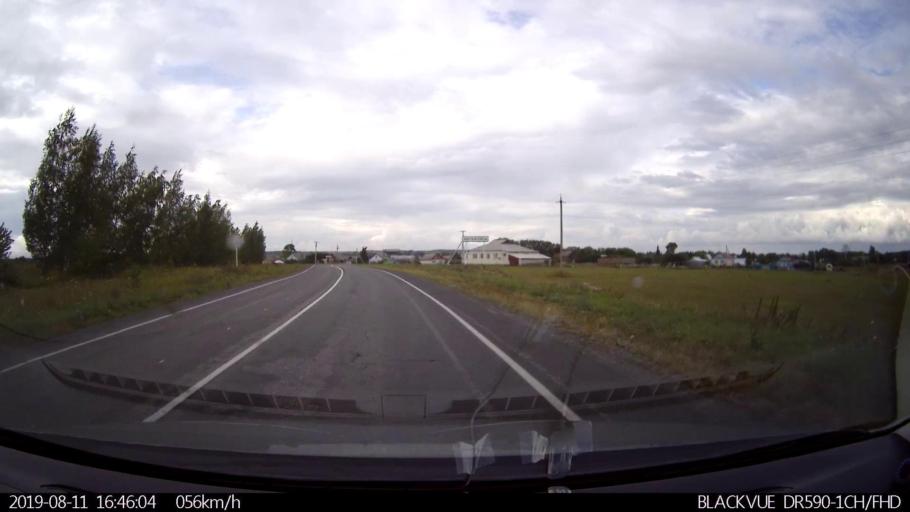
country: RU
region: Ulyanovsk
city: Mayna
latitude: 54.1954
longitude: 47.6880
